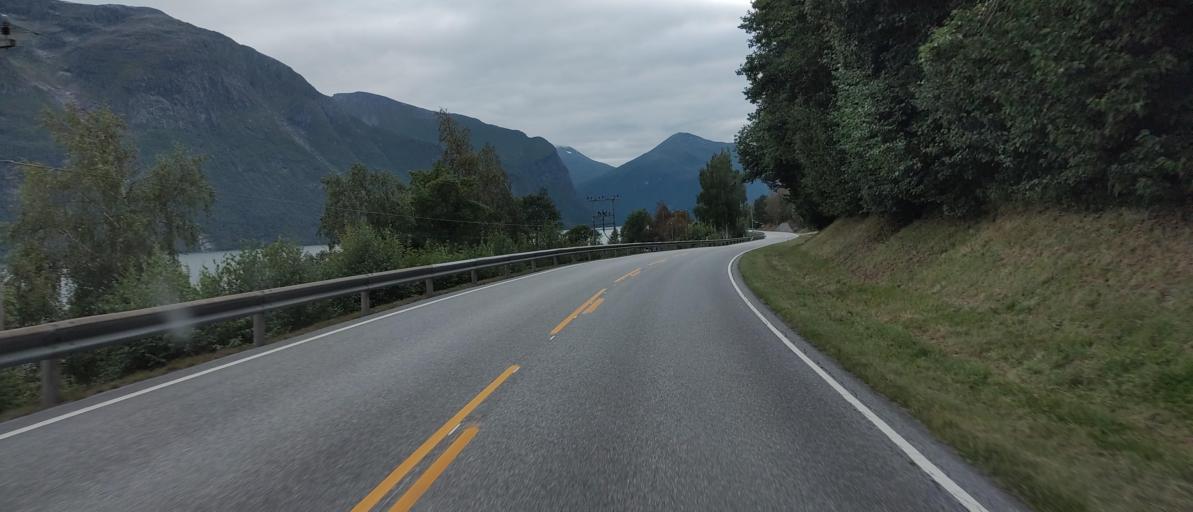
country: NO
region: More og Romsdal
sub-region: Rauma
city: Andalsnes
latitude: 62.5725
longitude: 7.6546
